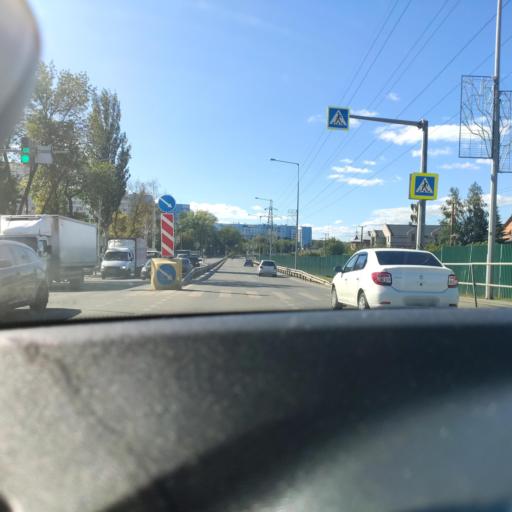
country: RU
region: Samara
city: Volzhskiy
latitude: 53.3501
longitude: 50.2183
